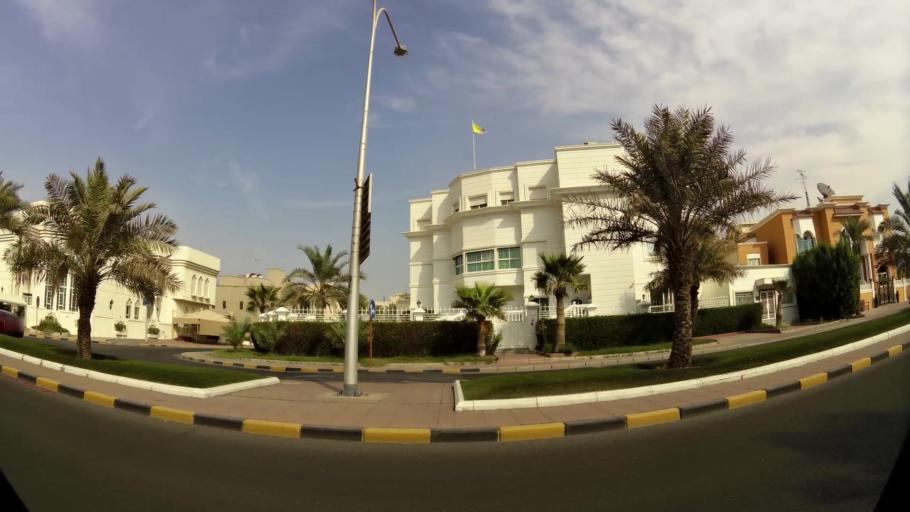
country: KW
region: Al Asimah
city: Ash Shamiyah
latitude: 29.3121
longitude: 47.9692
